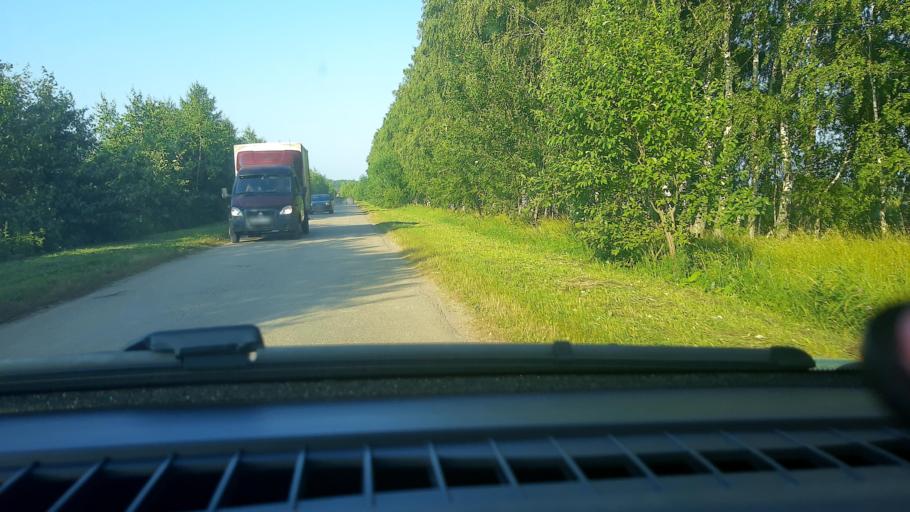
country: RU
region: Nizjnij Novgorod
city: Nizhniy Novgorod
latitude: 56.1943
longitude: 43.9526
